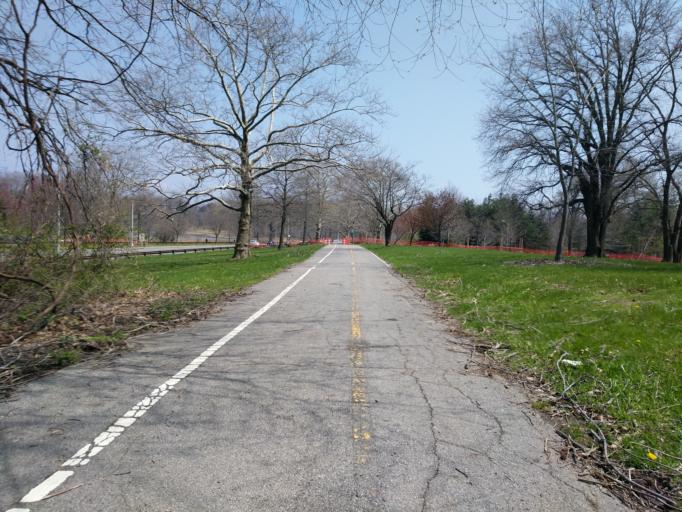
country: US
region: New York
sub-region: Westchester County
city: Pelham Manor
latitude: 40.8627
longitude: -73.8085
